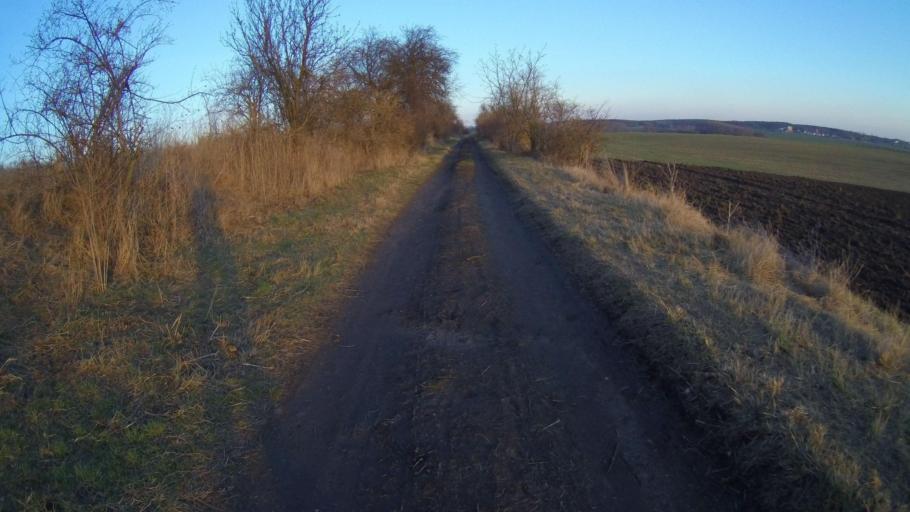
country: CZ
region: Ustecky
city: Roudnice nad Labem
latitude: 50.3756
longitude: 14.2909
